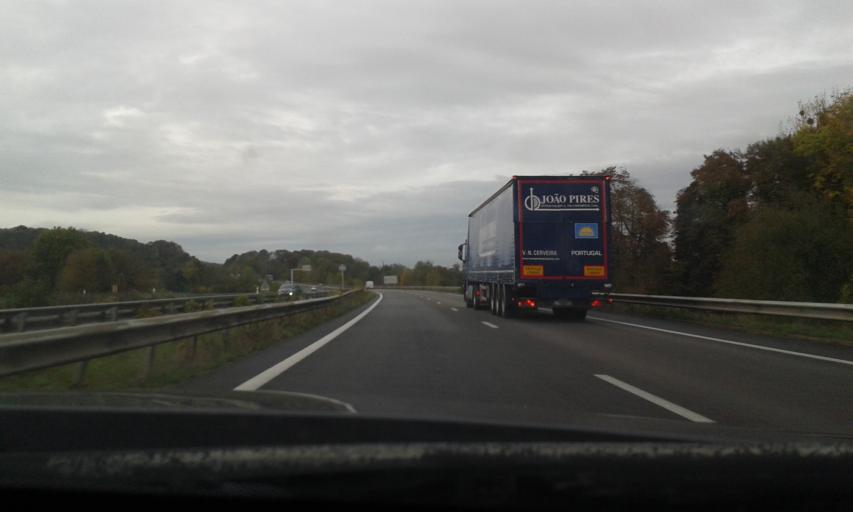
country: FR
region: Haute-Normandie
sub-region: Departement de l'Eure
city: Acquigny
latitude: 49.1572
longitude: 1.1817
